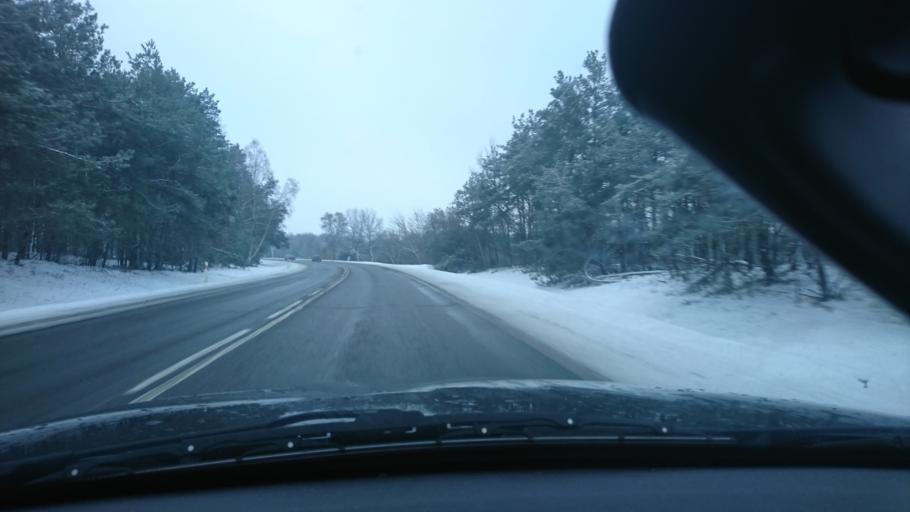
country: PL
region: Masovian Voivodeship
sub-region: Powiat ciechanowski
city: Glinojeck
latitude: 52.7556
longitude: 20.3127
